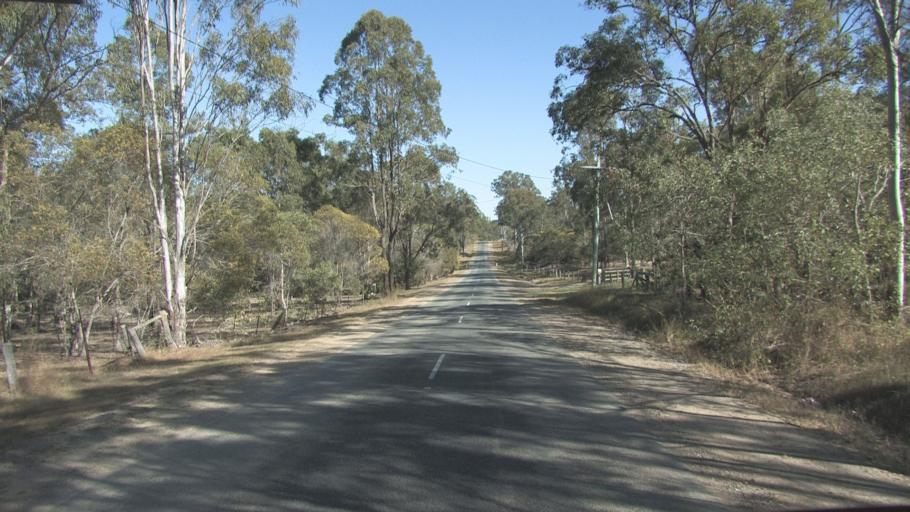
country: AU
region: Queensland
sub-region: Logan
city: Cedar Vale
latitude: -27.8425
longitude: 153.0452
